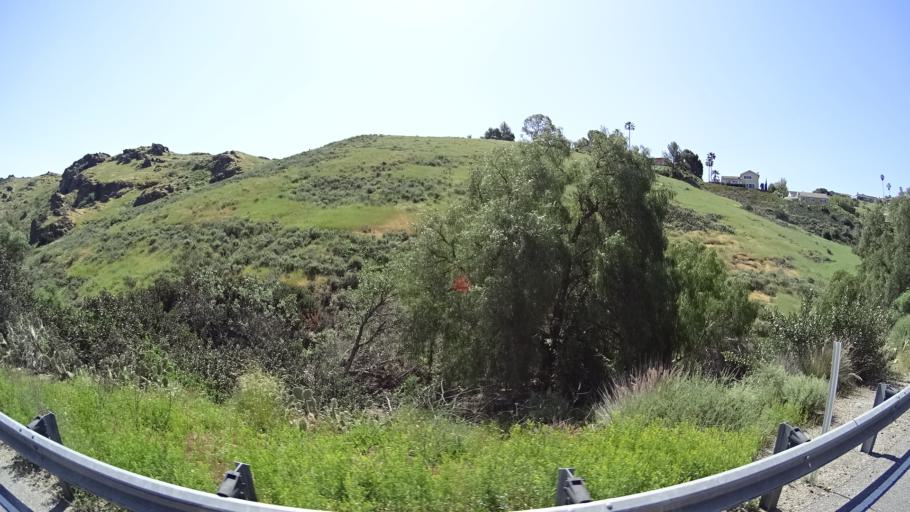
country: US
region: California
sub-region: Ventura County
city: Moorpark
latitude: 34.2353
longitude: -118.8639
